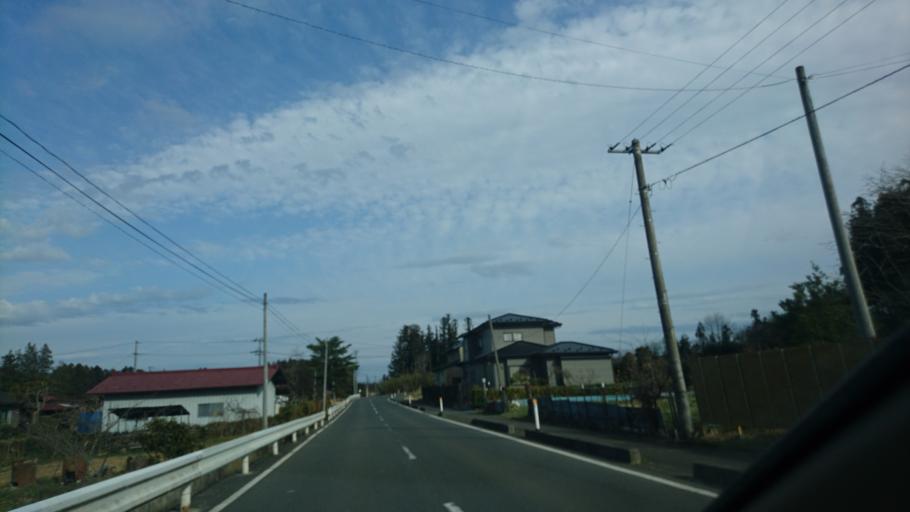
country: JP
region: Iwate
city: Ichinoseki
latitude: 38.8105
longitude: 141.0287
